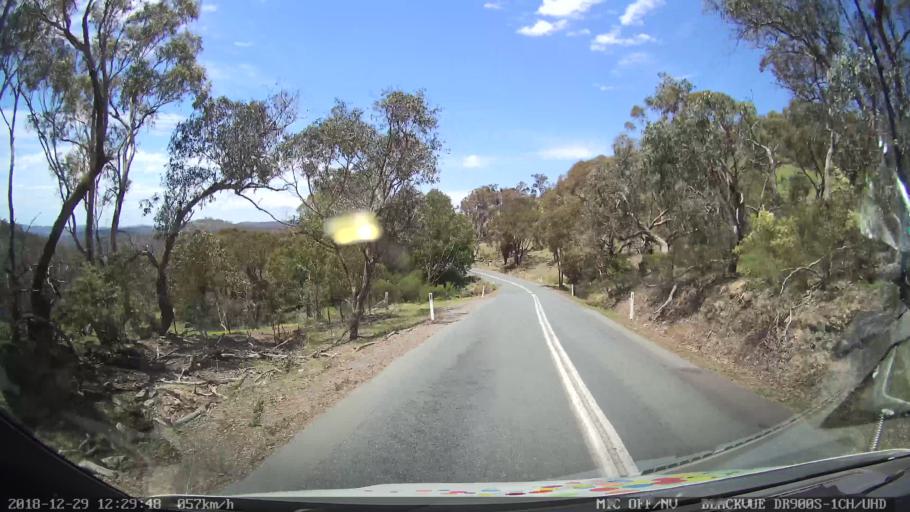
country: AU
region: Australian Capital Territory
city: Macarthur
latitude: -35.5009
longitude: 149.2316
